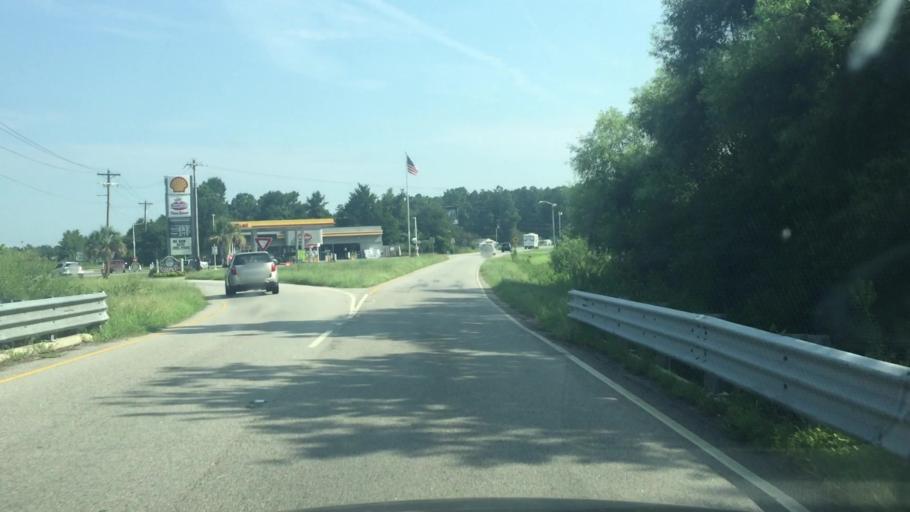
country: US
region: North Carolina
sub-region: Columbus County
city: Tabor City
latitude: 34.1326
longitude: -78.8758
